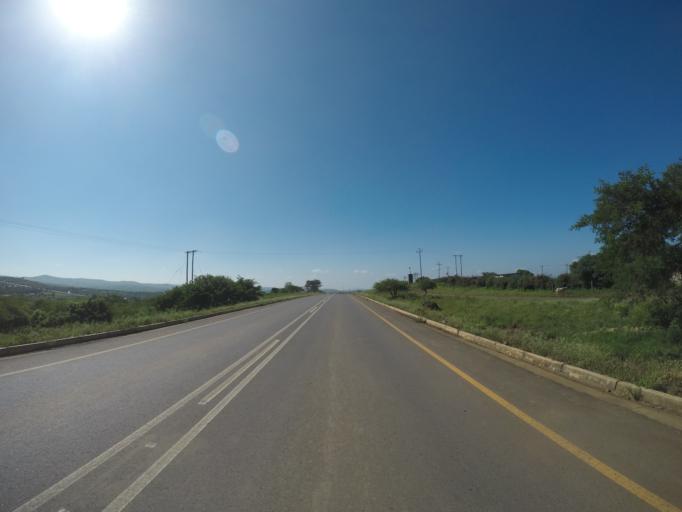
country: ZA
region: KwaZulu-Natal
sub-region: uThungulu District Municipality
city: Empangeni
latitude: -28.5666
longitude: 31.7092
